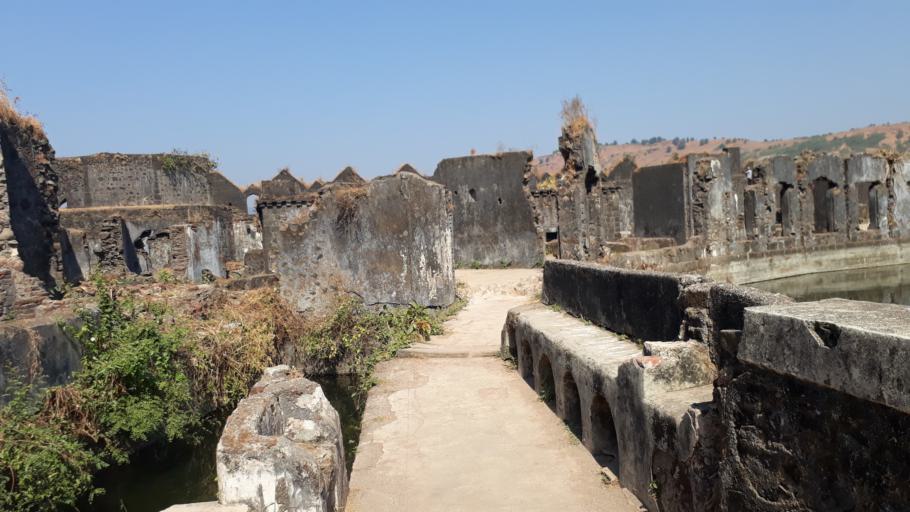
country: IN
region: Maharashtra
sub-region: Raigarh
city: Murud
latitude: 18.3006
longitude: 72.9646
